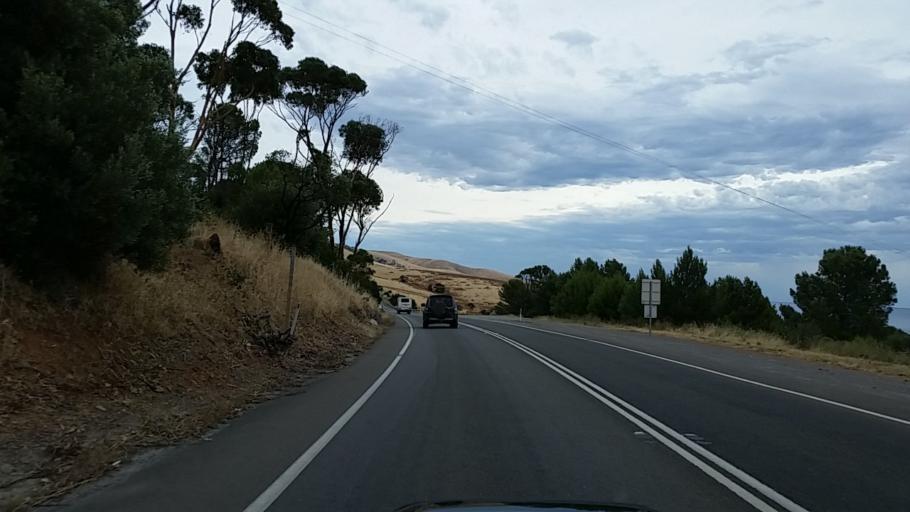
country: AU
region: South Australia
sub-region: Onkaparinga
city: Aldinga
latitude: -35.3390
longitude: 138.4637
